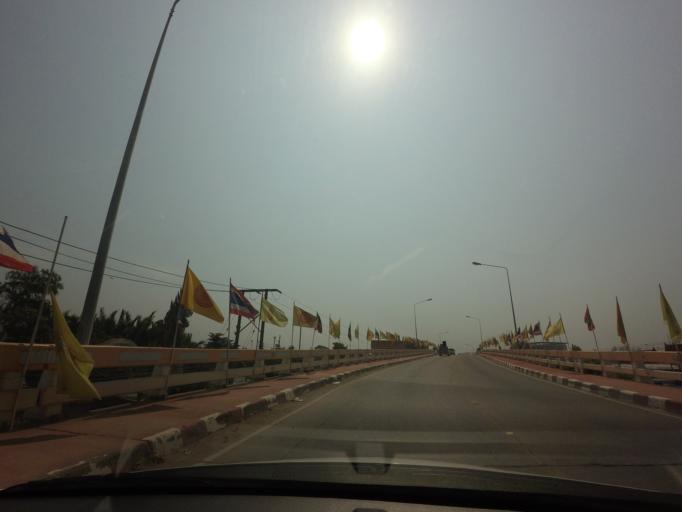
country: TH
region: Nakhon Pathom
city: Sam Phran
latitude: 13.7445
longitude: 100.2604
